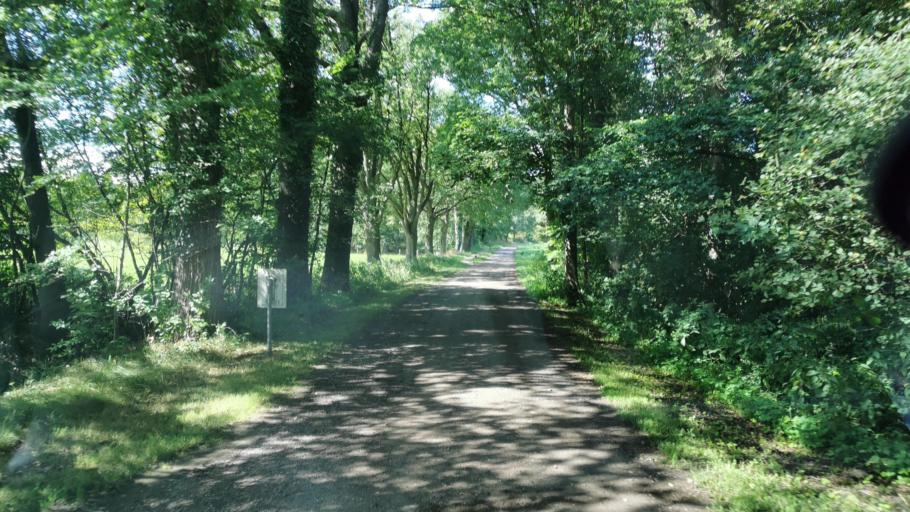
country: NL
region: Overijssel
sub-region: Gemeente Oldenzaal
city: Oldenzaal
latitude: 52.2793
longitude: 6.9578
